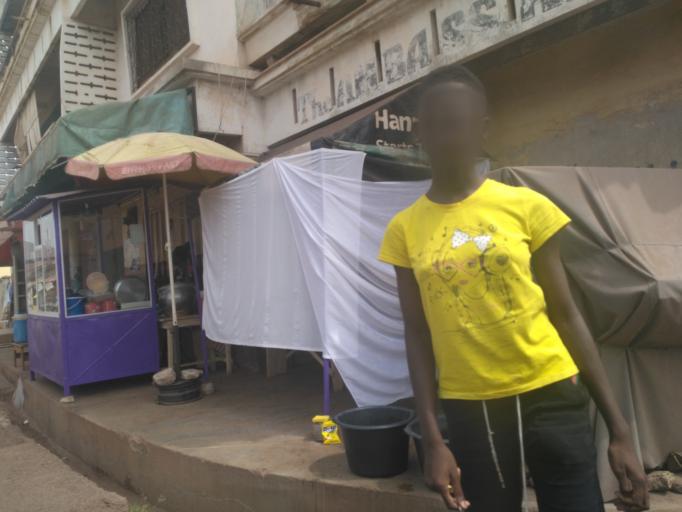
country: GH
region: Ashanti
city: Kumasi
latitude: 6.7065
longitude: -1.6217
